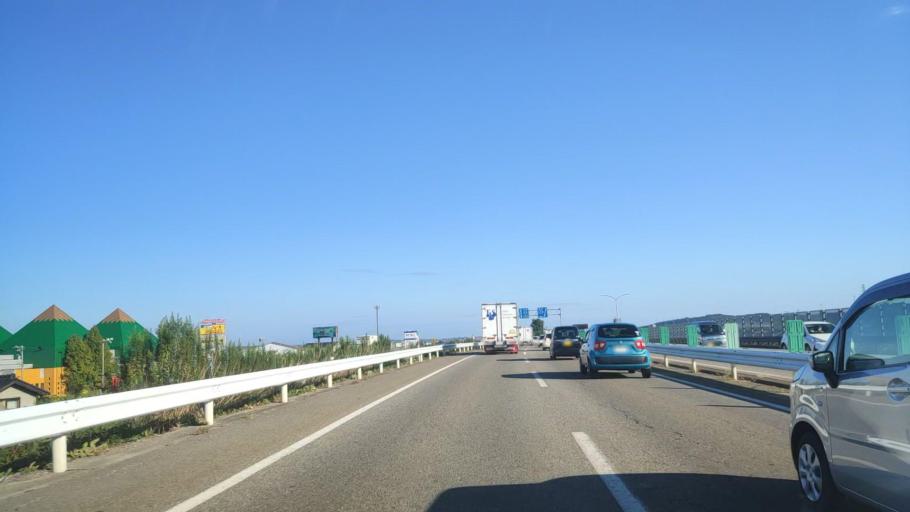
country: JP
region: Ishikawa
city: Tsubata
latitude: 36.6770
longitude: 136.7232
